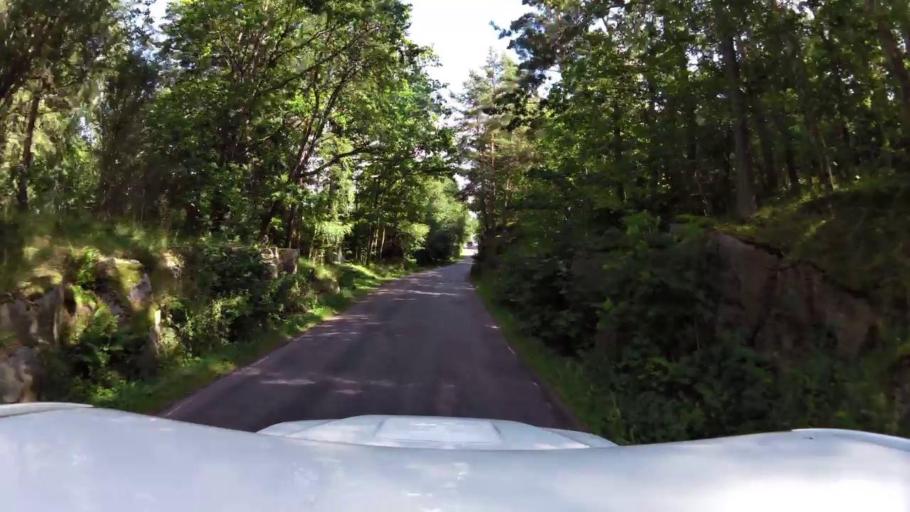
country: SE
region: OEstergoetland
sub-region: Kinda Kommun
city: Rimforsa
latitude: 58.2293
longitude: 15.6978
